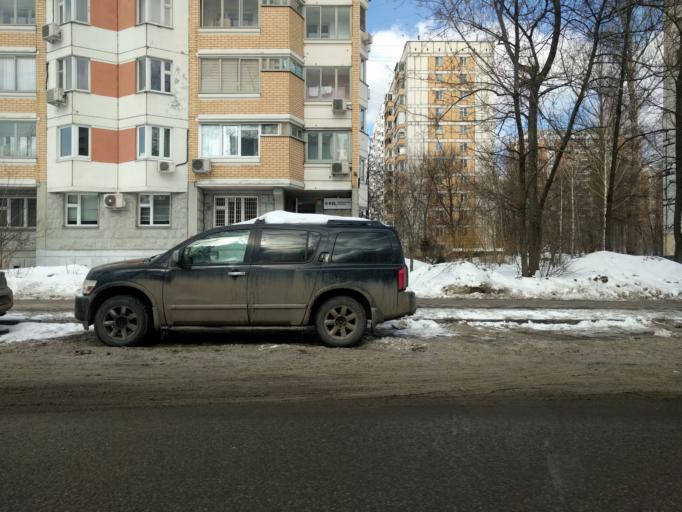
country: RU
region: Moscow
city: Gol'yanovo
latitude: 55.8033
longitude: 37.8138
